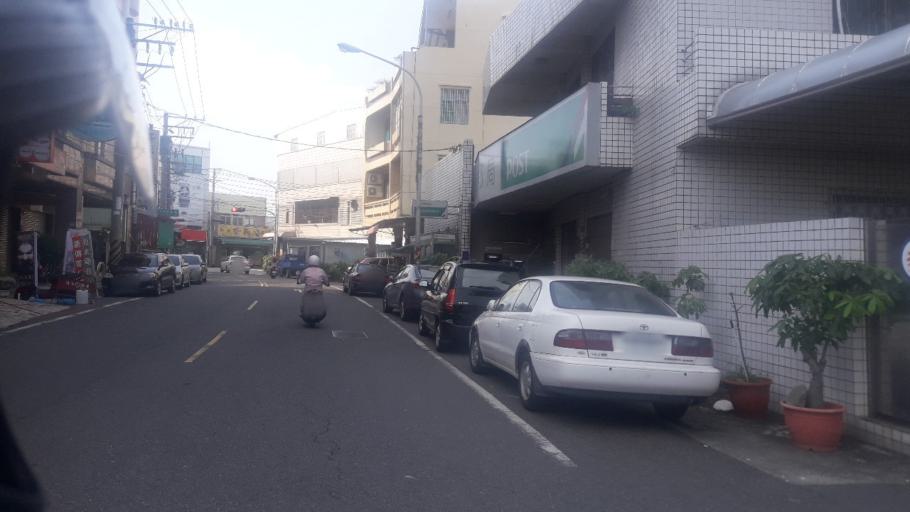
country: TW
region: Taiwan
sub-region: Tainan
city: Tainan
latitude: 22.8606
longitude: 120.2610
